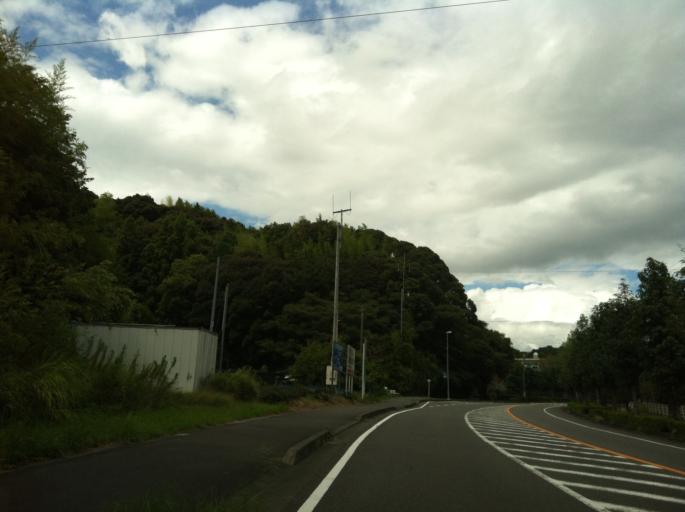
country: JP
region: Shizuoka
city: Kakegawa
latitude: 34.7073
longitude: 138.0464
